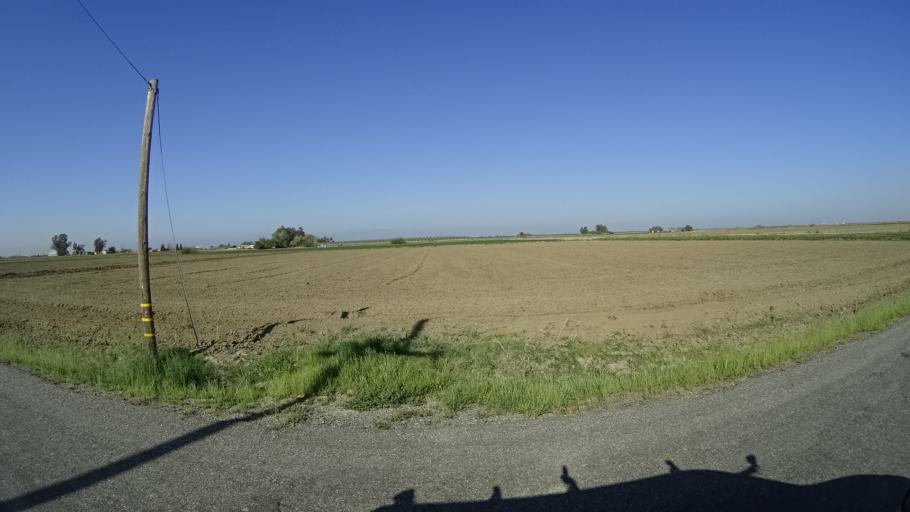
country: US
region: California
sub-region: Glenn County
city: Willows
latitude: 39.5777
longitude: -122.1076
